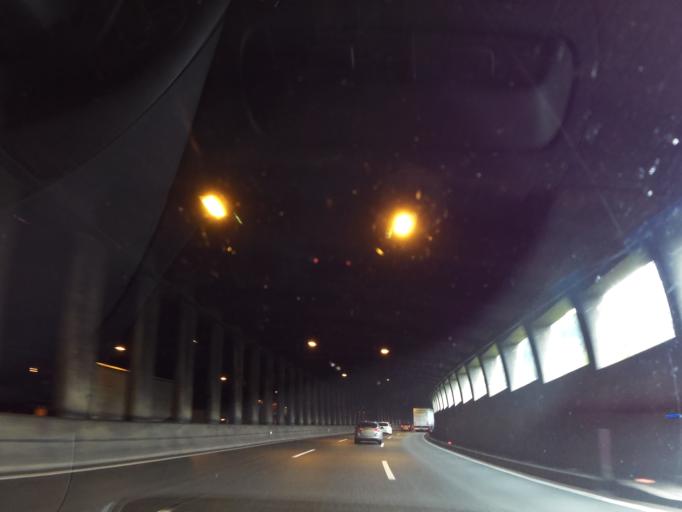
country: AT
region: Tyrol
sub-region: Politischer Bezirk Innsbruck Land
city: Schoenberg im Stubaital
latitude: 47.1894
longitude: 11.4013
